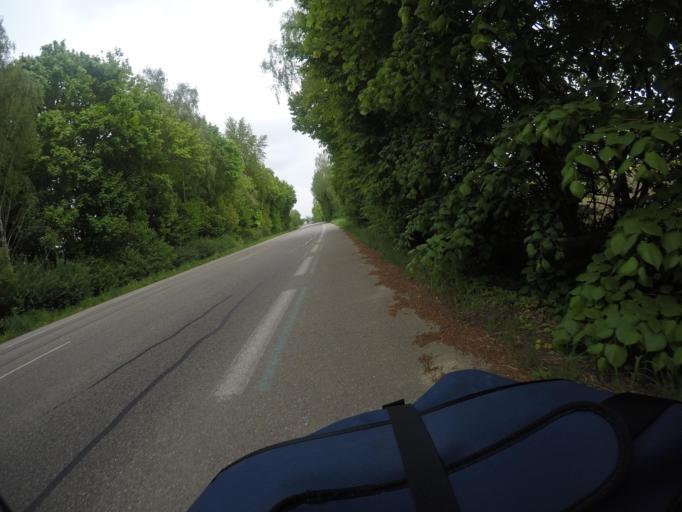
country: FR
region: Alsace
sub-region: Departement du Bas-Rhin
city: Kilstett
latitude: 48.6827
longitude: 7.8657
